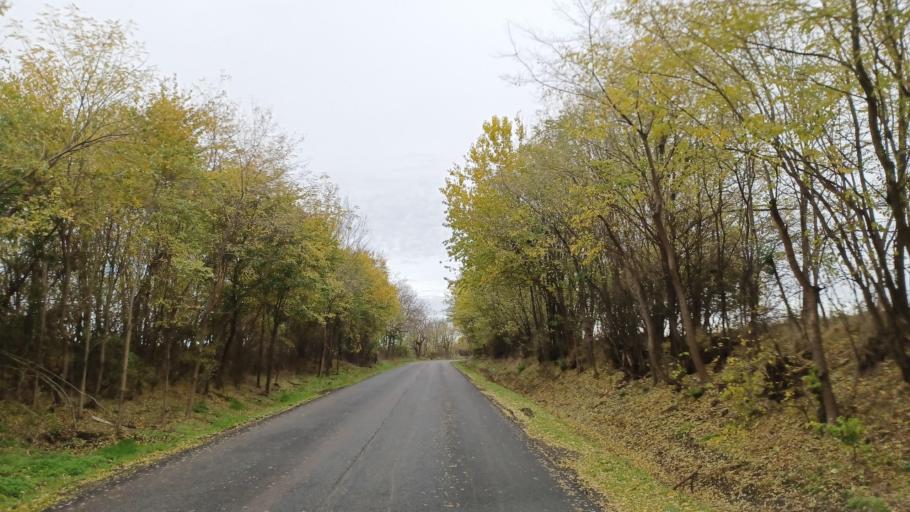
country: HU
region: Tolna
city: Tengelic
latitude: 46.5358
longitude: 18.7591
